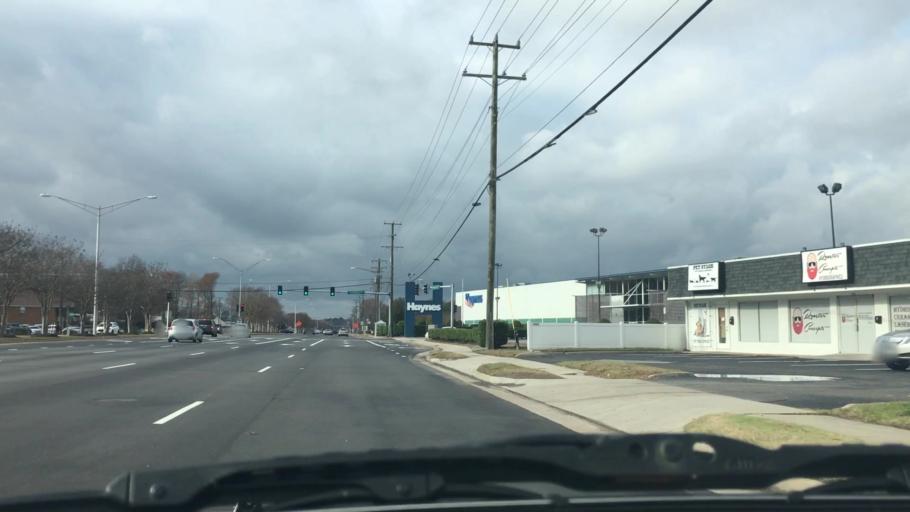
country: US
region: Virginia
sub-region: City of Chesapeake
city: Chesapeake
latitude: 36.8486
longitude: -76.1633
